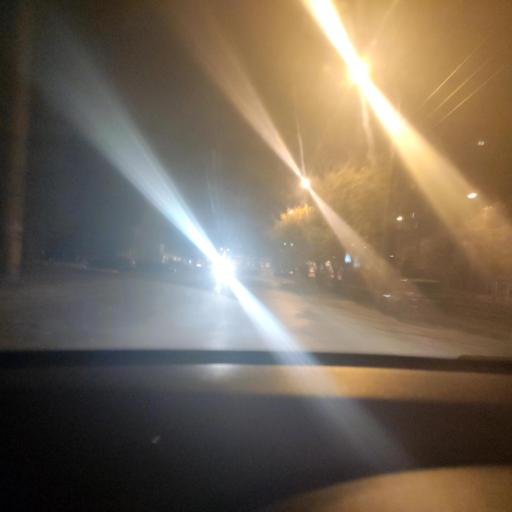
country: RU
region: Samara
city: Samara
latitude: 53.2007
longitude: 50.1485
